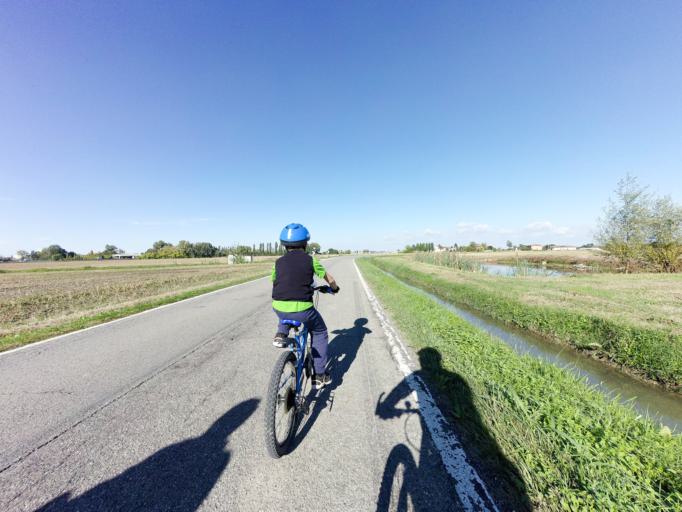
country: IT
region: Emilia-Romagna
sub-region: Provincia di Bologna
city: Progresso
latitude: 44.5782
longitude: 11.3963
